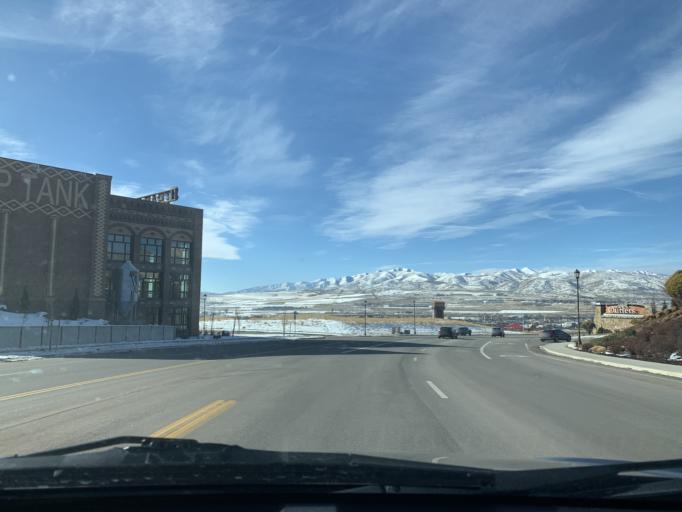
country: US
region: Utah
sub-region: Utah County
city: Lehi
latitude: 40.4332
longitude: -111.8839
